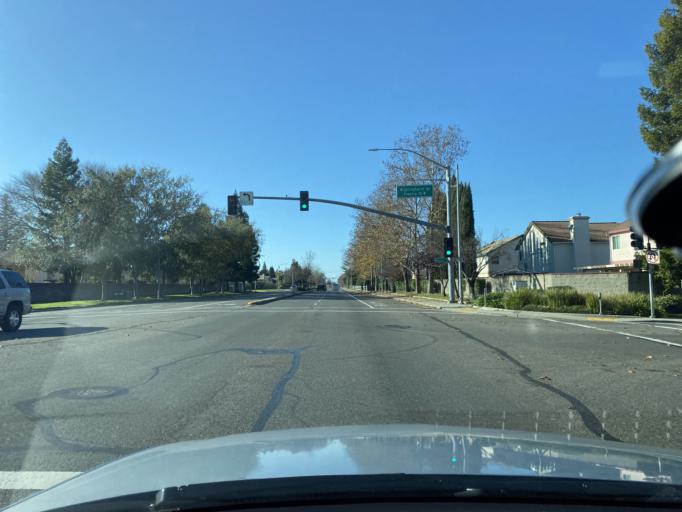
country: US
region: California
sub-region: Sacramento County
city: Elk Grove
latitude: 38.4381
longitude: -121.3796
